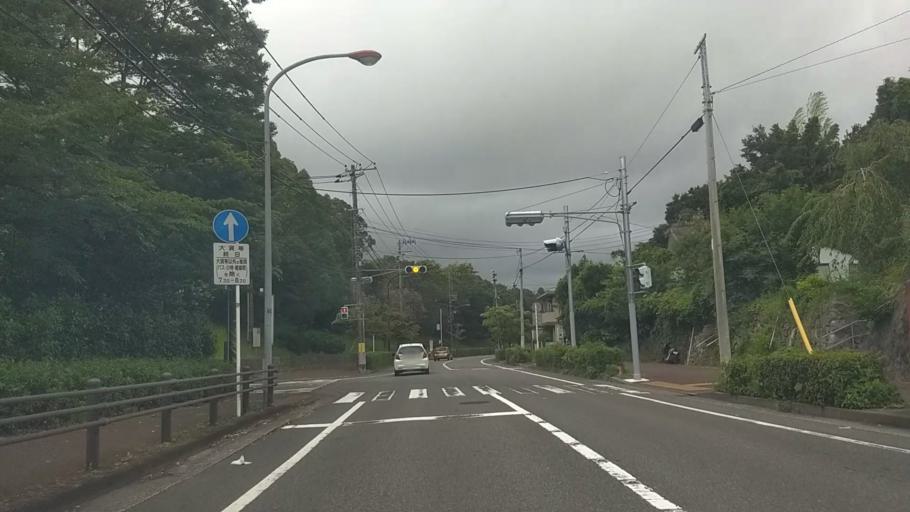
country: JP
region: Kanagawa
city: Yokosuka
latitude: 35.2688
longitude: 139.6671
